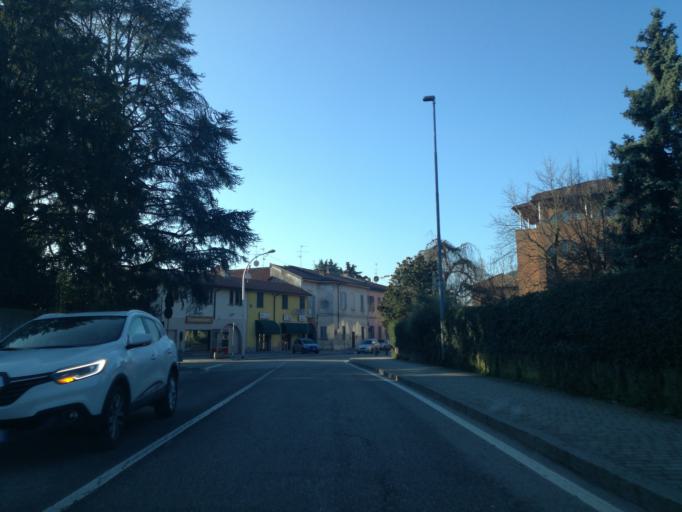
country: IT
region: Lombardy
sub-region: Provincia di Monza e Brianza
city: Bernareggio
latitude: 45.6501
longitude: 9.4074
